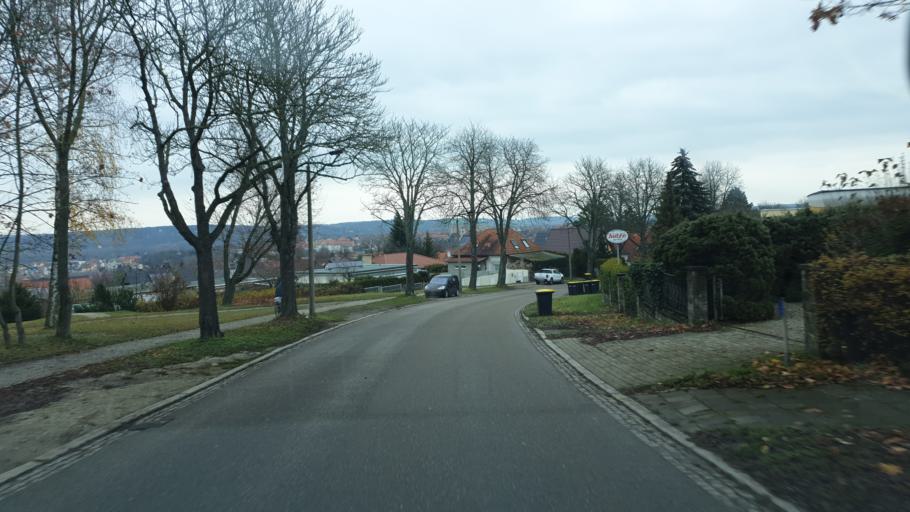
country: DE
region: Saxony-Anhalt
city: Naumburg
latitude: 51.1469
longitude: 11.7910
